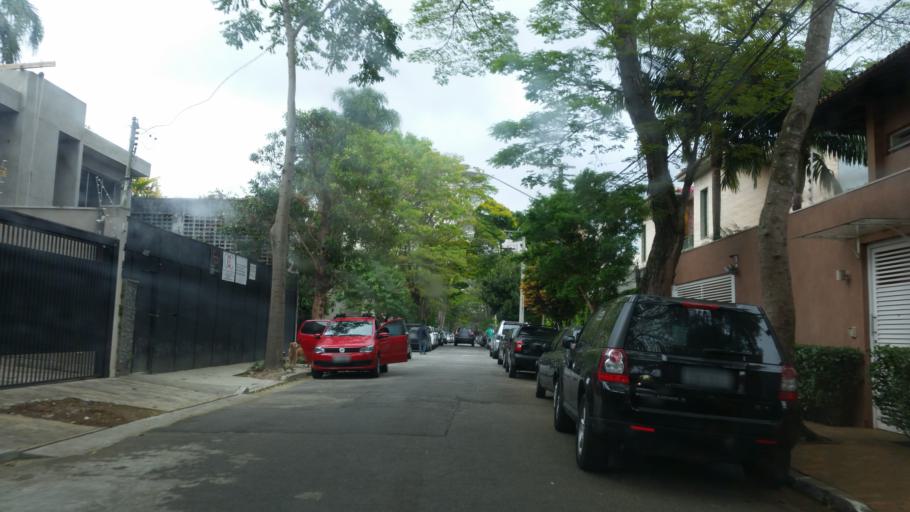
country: BR
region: Sao Paulo
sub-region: Sao Paulo
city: Sao Paulo
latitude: -23.5954
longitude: -46.6596
